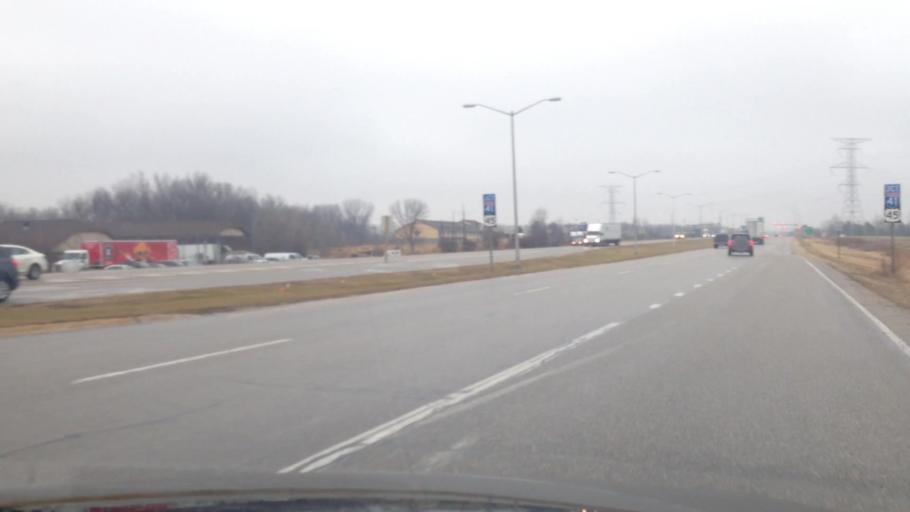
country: US
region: Wisconsin
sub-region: Washington County
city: Germantown
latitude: 43.2179
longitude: -88.1432
